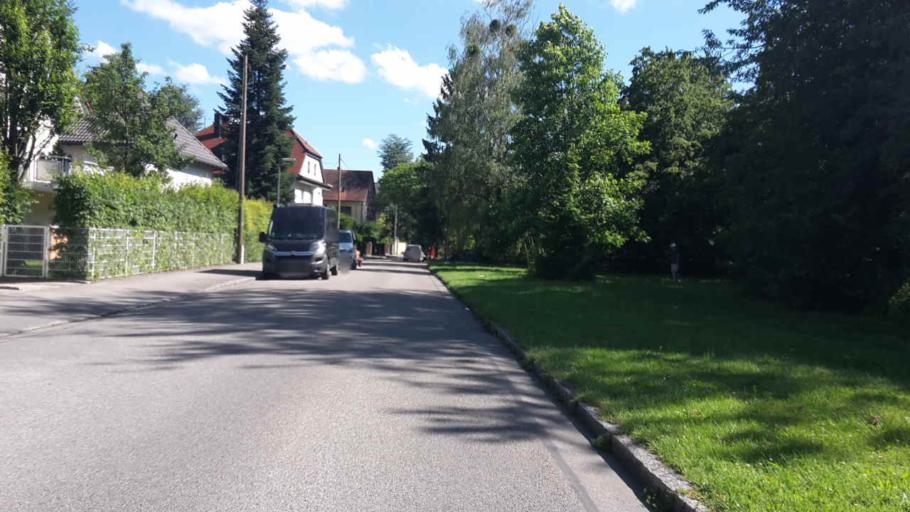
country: DE
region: Bavaria
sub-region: Upper Bavaria
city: Pasing
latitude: 48.1668
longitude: 11.4700
